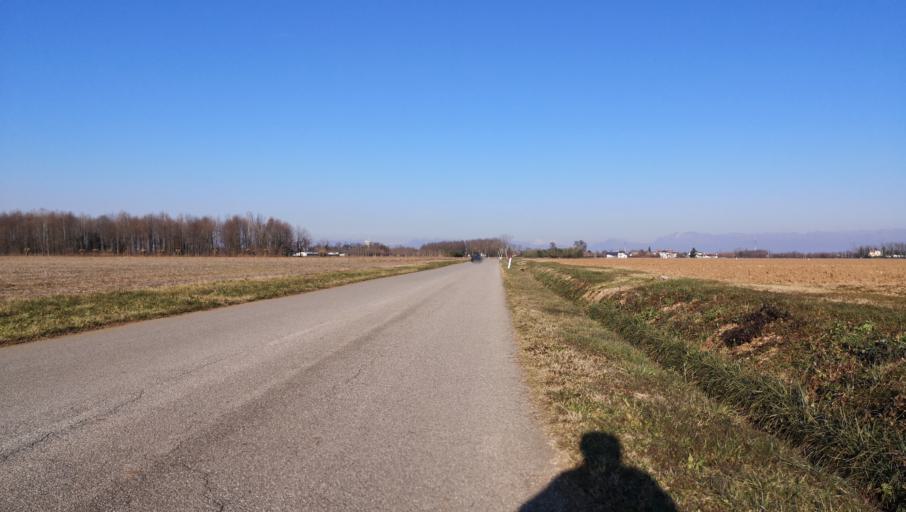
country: IT
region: Friuli Venezia Giulia
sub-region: Provincia di Udine
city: Santa Maria la Longa
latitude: 45.9459
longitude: 13.2747
